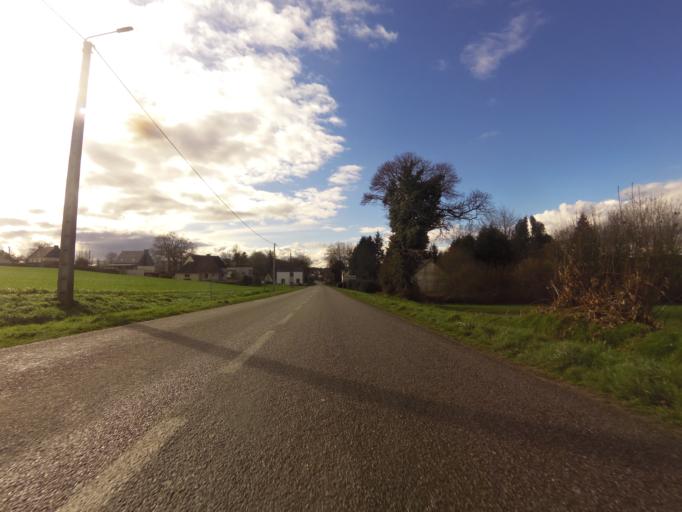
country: FR
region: Brittany
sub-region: Departement du Morbihan
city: Serent
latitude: 47.8278
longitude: -2.4950
